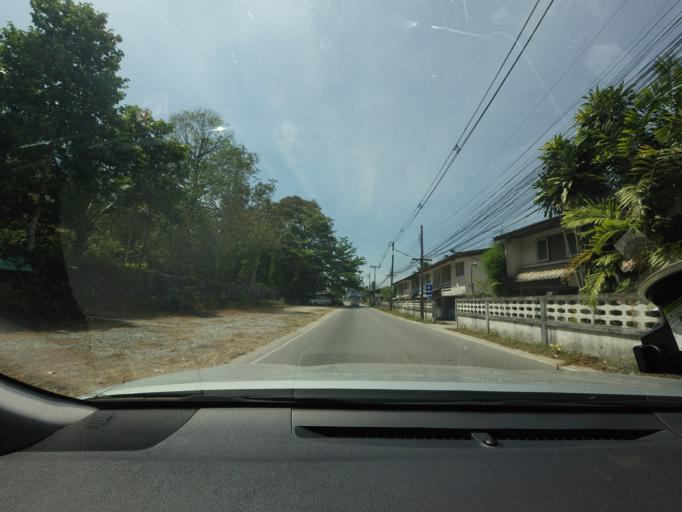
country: TH
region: Narathiwat
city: Narathiwat
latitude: 6.4436
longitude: 101.8053
